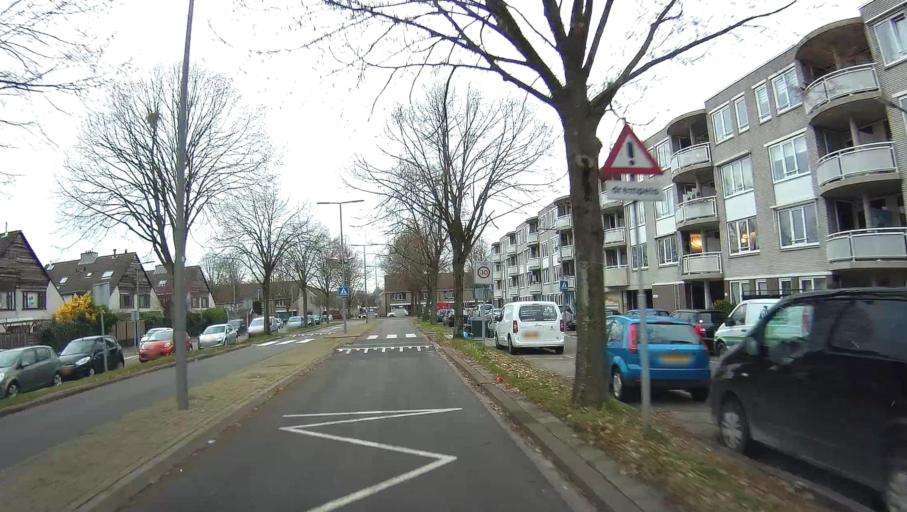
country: NL
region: South Holland
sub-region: Gemeente Capelle aan den IJssel
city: Capelle aan den IJssel
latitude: 51.9692
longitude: 4.5764
